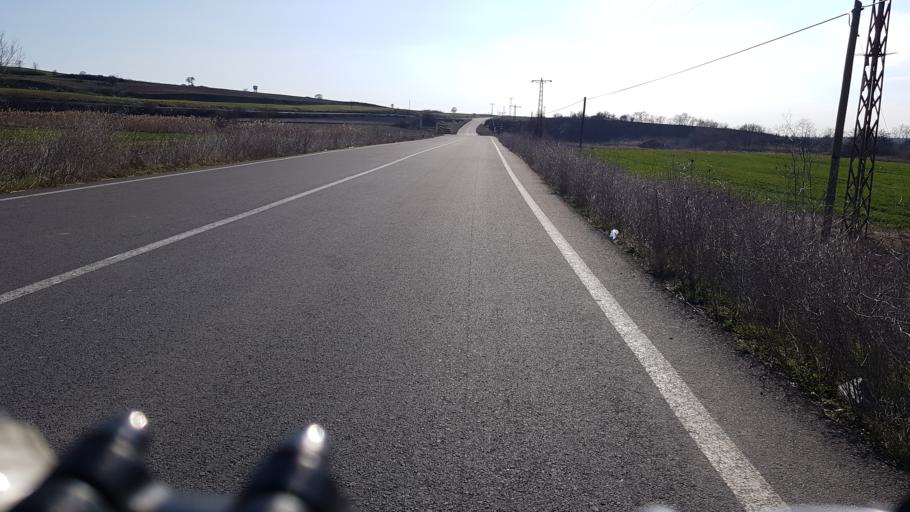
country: TR
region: Tekirdag
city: Velimese
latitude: 41.3584
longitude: 27.8519
